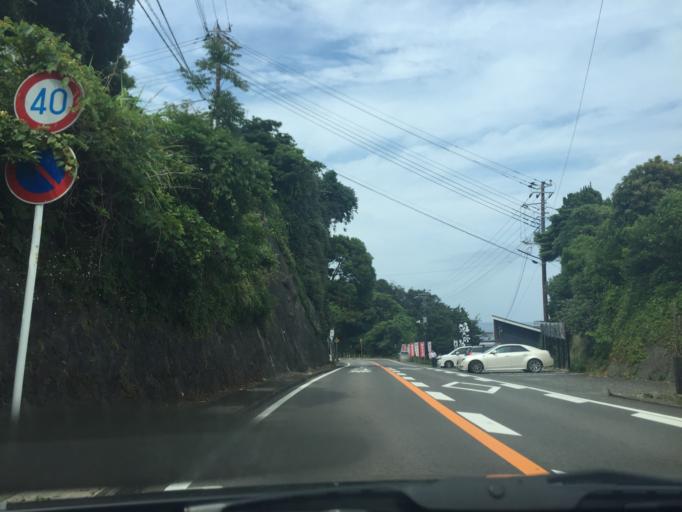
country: JP
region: Shizuoka
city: Shimoda
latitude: 34.7046
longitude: 138.9772
